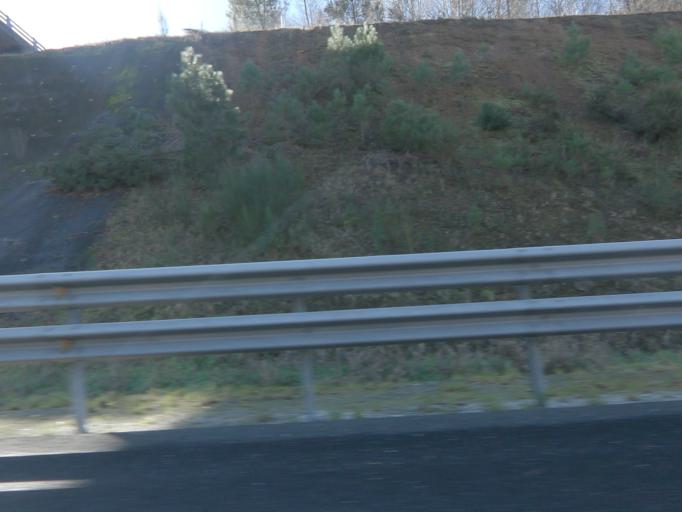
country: ES
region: Galicia
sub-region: Provincia de Pontevedra
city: Lalin
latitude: 42.6322
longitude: -8.1248
